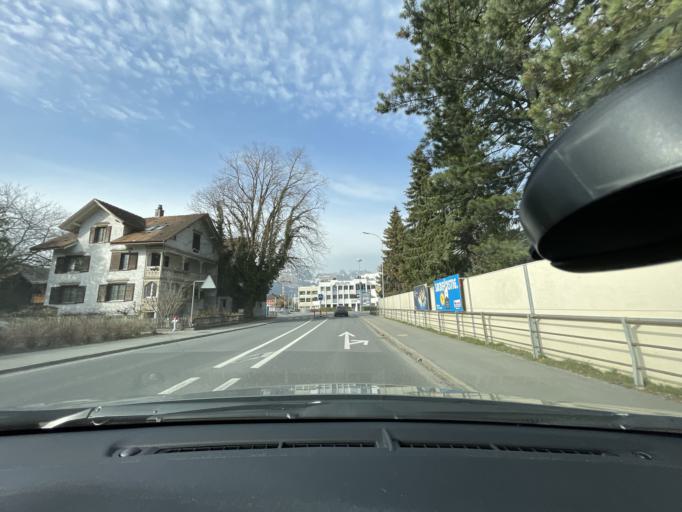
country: CH
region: Saint Gallen
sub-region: Wahlkreis Werdenberg
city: Buchs
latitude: 47.1587
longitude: 9.4774
